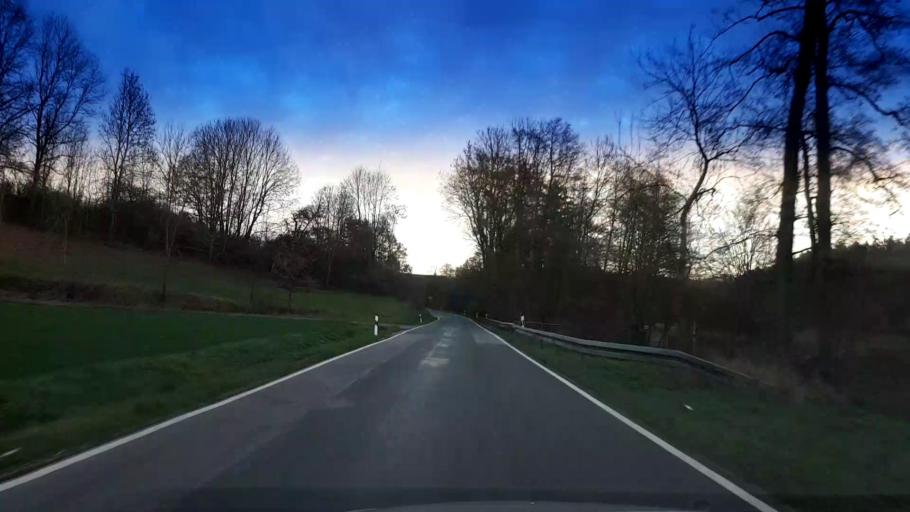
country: DE
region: Bavaria
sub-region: Upper Franconia
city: Walsdorf
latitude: 49.8789
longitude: 10.7628
